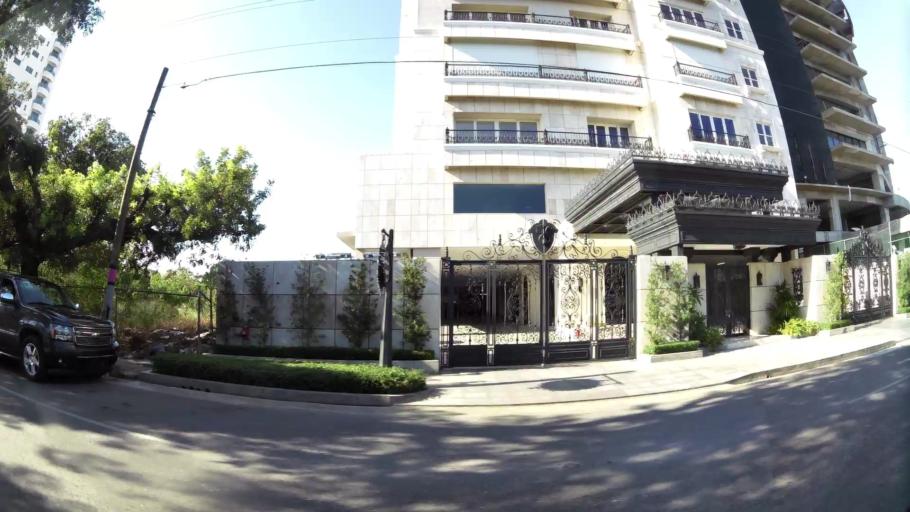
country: DO
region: Nacional
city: Bella Vista
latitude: 18.4373
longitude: -69.9744
